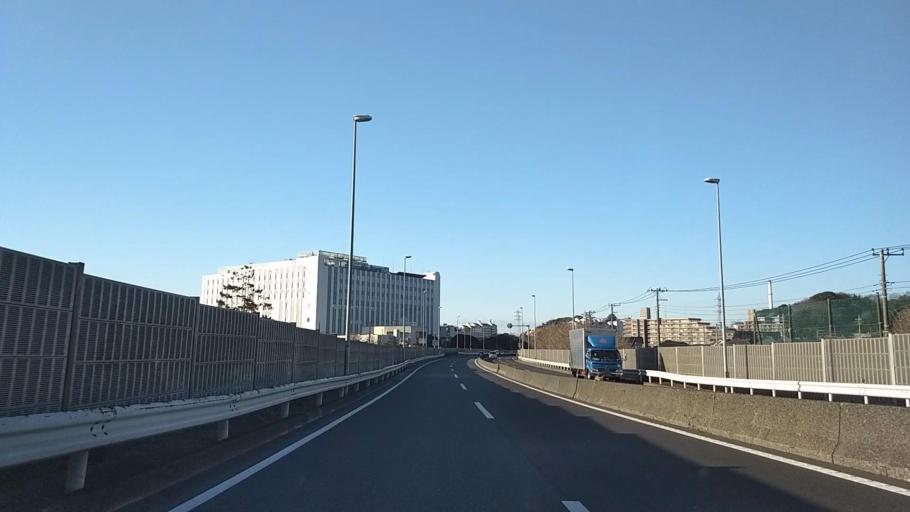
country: JP
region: Kanagawa
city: Fujisawa
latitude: 35.3534
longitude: 139.4847
